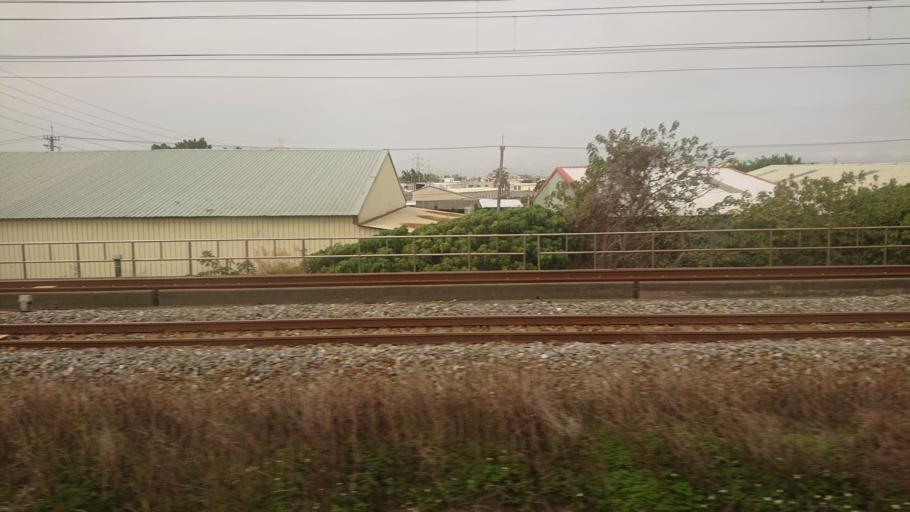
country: TW
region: Taiwan
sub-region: Changhua
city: Chang-hua
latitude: 24.1110
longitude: 120.5785
